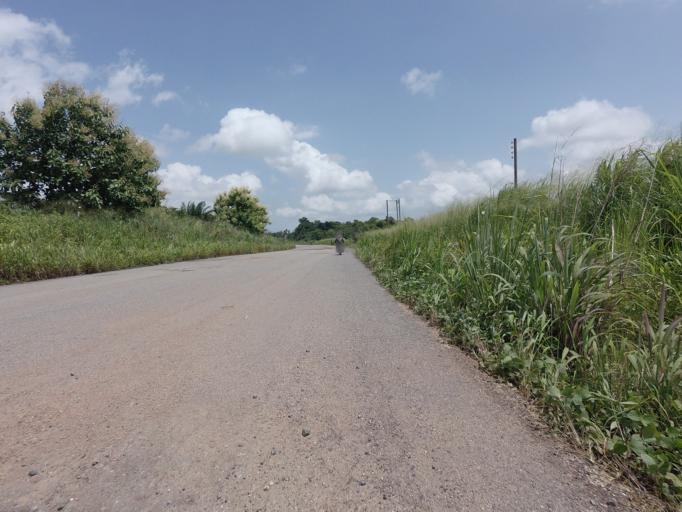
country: GH
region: Volta
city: Kpandu
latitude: 6.8670
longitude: 0.4042
